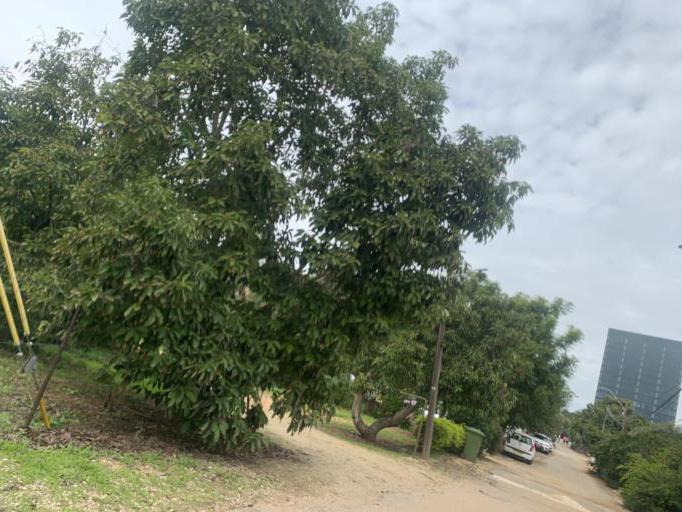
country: IL
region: Central District
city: Hod HaSharon
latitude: 32.1704
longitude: 34.8912
